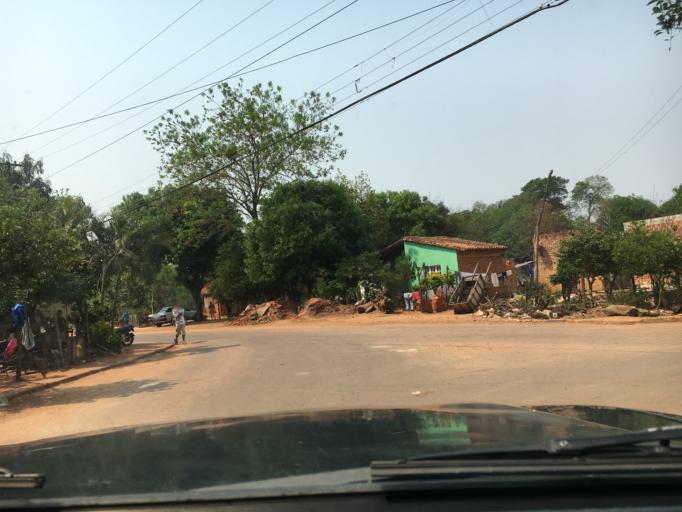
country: PY
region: Central
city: Villa Elisa
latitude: -25.3821
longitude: -57.5708
